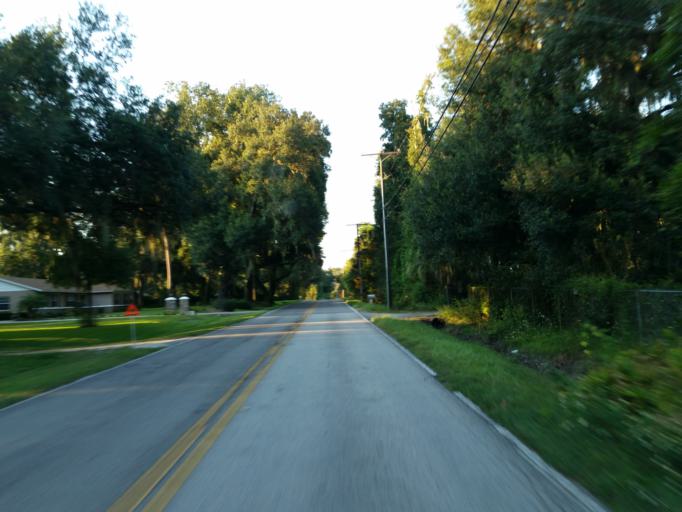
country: US
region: Florida
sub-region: Hillsborough County
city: Dover
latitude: 28.0296
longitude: -82.2447
